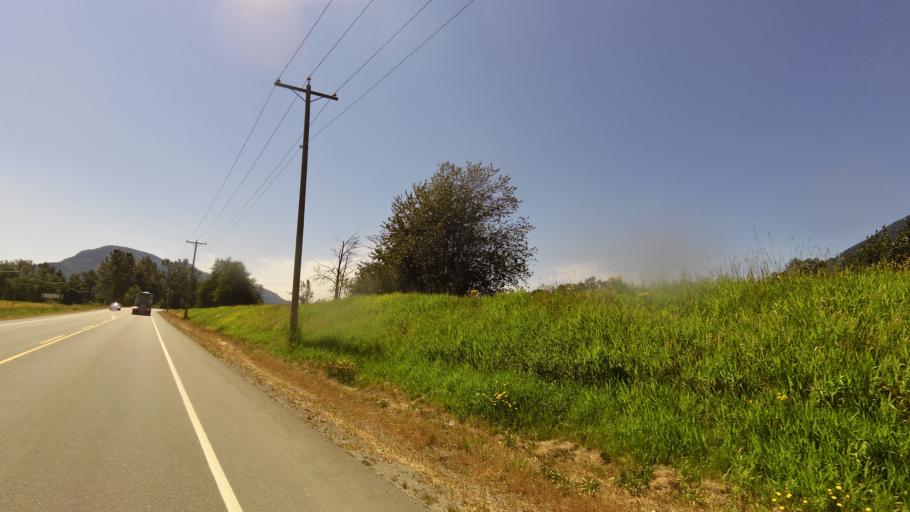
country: CA
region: British Columbia
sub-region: Fraser Valley Regional District
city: Chilliwack
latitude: 49.1818
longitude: -122.0711
